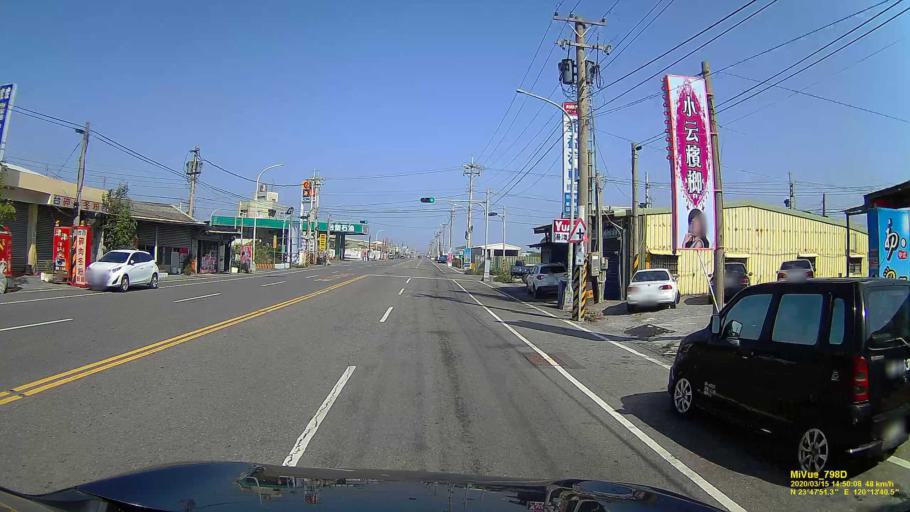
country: TW
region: Taiwan
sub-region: Yunlin
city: Douliu
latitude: 23.7976
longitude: 120.2281
